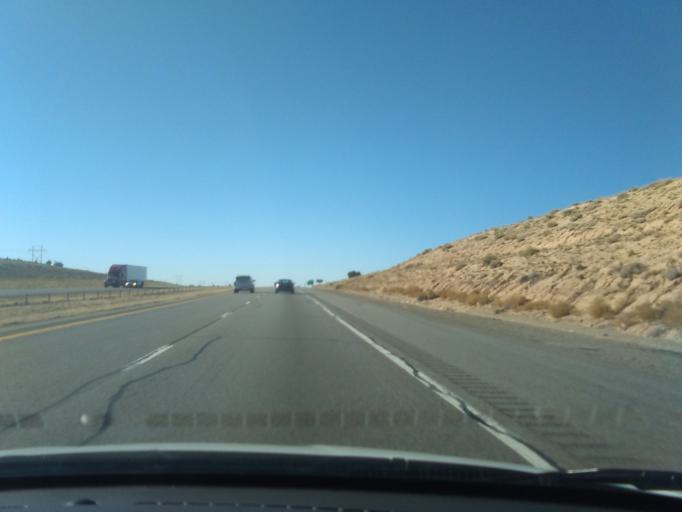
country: US
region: New Mexico
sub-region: Sandoval County
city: San Felipe Pueblo
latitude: 35.4322
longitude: -106.3820
